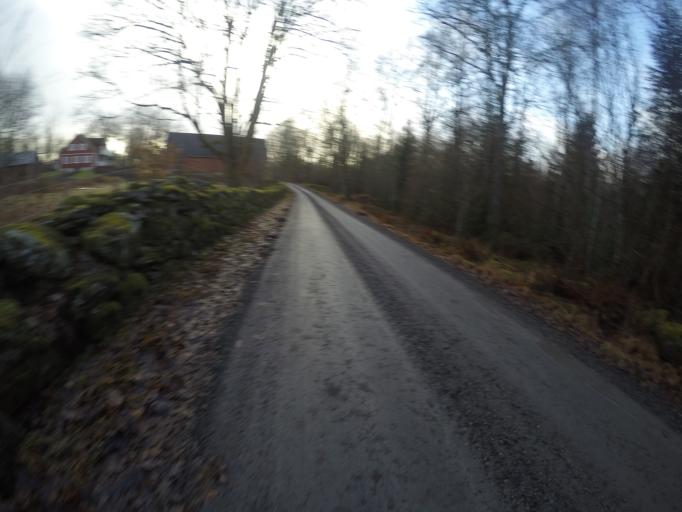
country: SE
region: Skane
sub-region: Osby Kommun
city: Lonsboda
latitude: 56.3788
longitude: 14.3383
